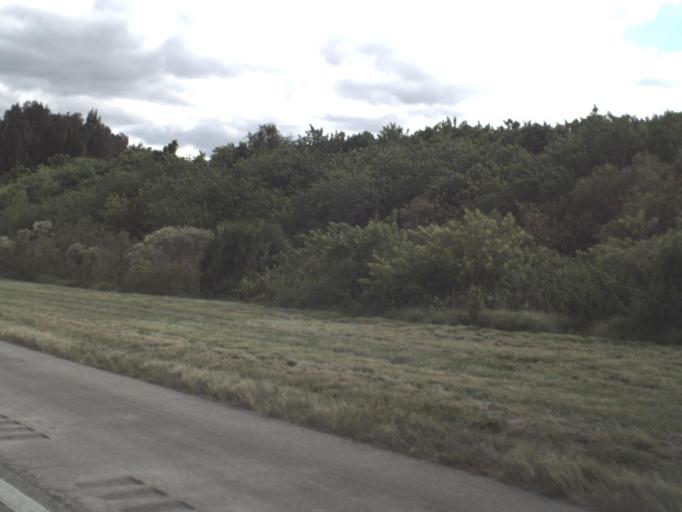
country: US
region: Florida
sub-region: Saint Lucie County
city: Fort Pierce South
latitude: 27.4182
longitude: -80.4061
